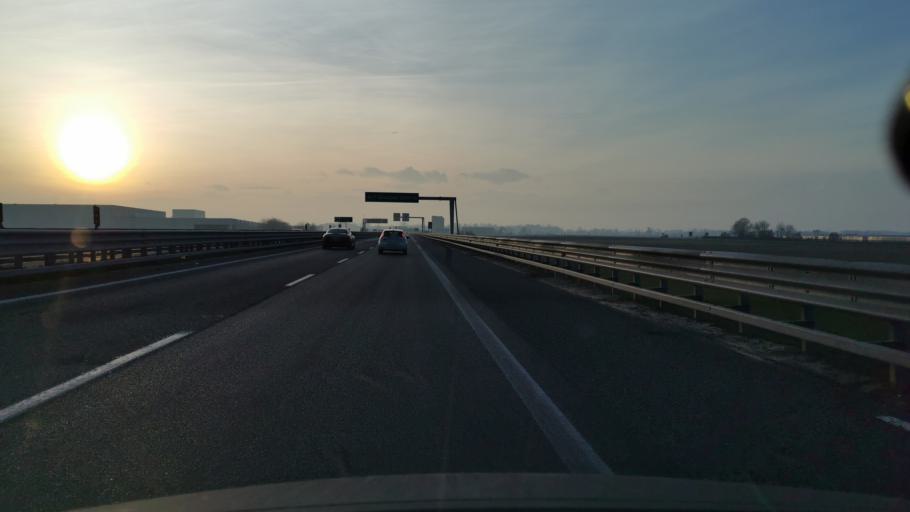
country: IT
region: Piedmont
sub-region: Provincia di Cuneo
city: Cervere
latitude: 44.6645
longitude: 7.7948
